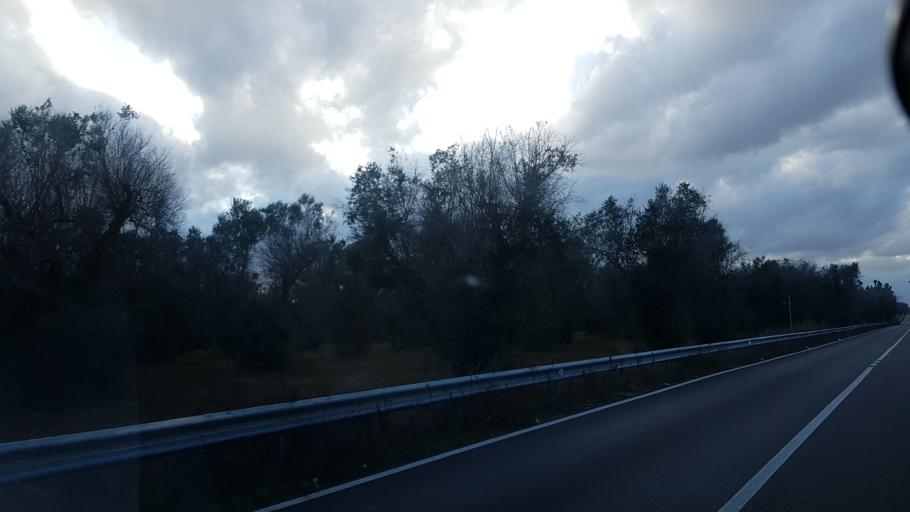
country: IT
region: Apulia
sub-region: Provincia di Brindisi
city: Torchiarolo
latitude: 40.4870
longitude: 18.0324
